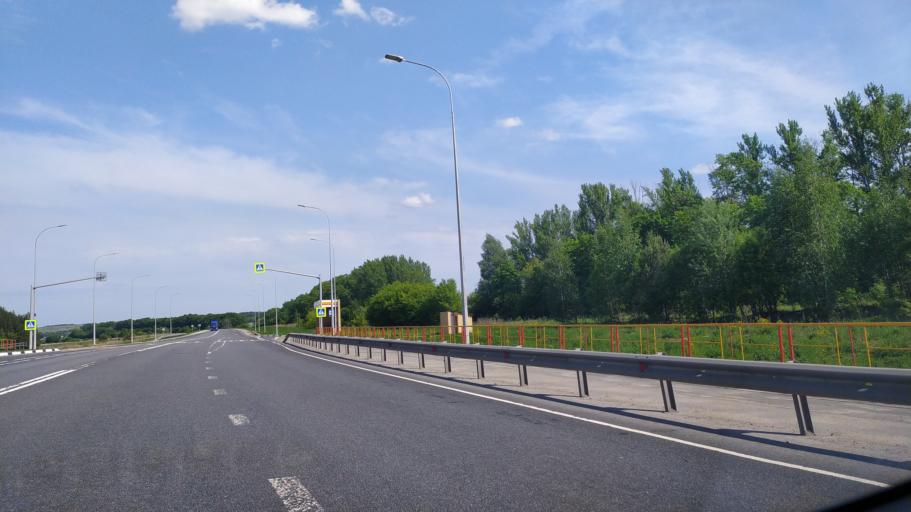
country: RU
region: Chuvashia
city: Kozlovka
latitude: 55.7848
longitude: 48.1575
